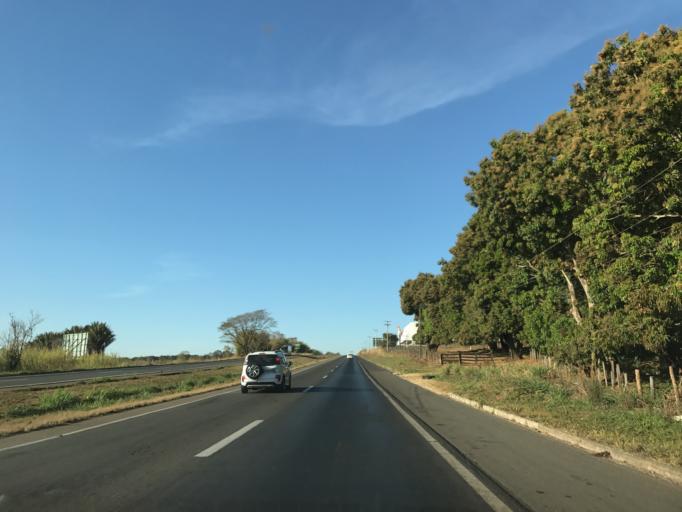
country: BR
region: Goias
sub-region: Aparecida De Goiania
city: Aparecida de Goiania
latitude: -16.8509
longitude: -49.2473
